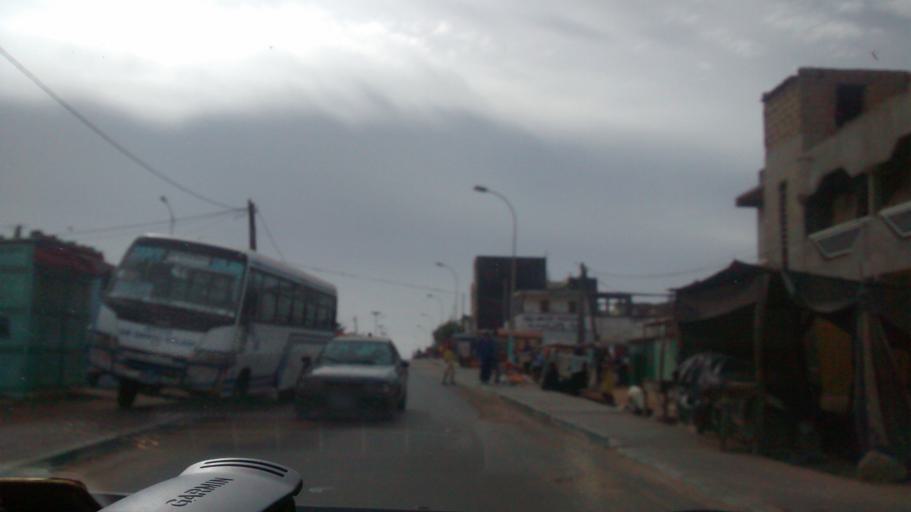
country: SN
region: Dakar
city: Pikine
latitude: 14.7829
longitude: -17.3821
